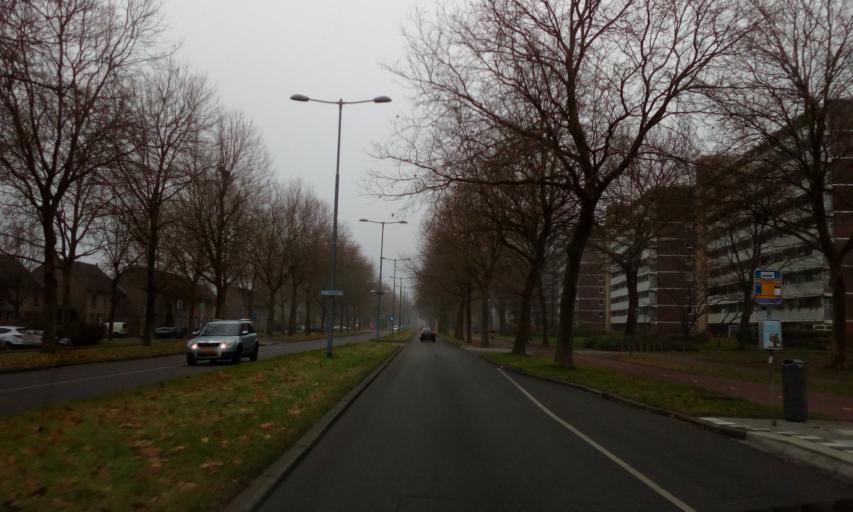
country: NL
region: South Holland
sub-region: Gemeente Rotterdam
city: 's-Gravenland
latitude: 51.9570
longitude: 4.5322
